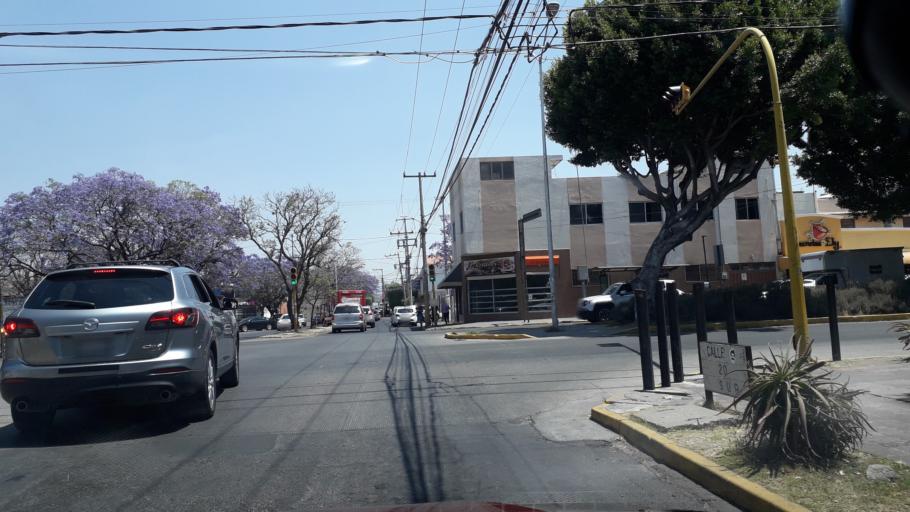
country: MX
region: Puebla
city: Puebla
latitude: 19.0257
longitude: -98.1924
